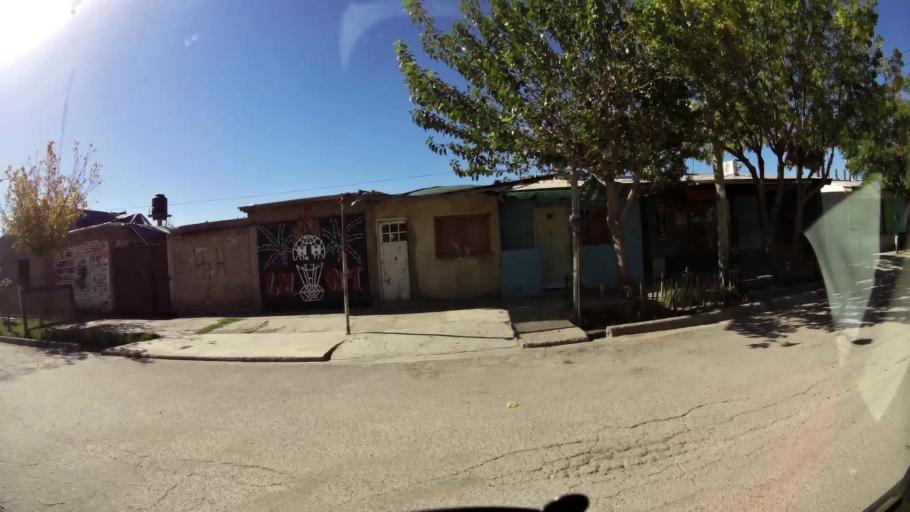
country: AR
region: Mendoza
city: Las Heras
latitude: -32.8386
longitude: -68.8145
